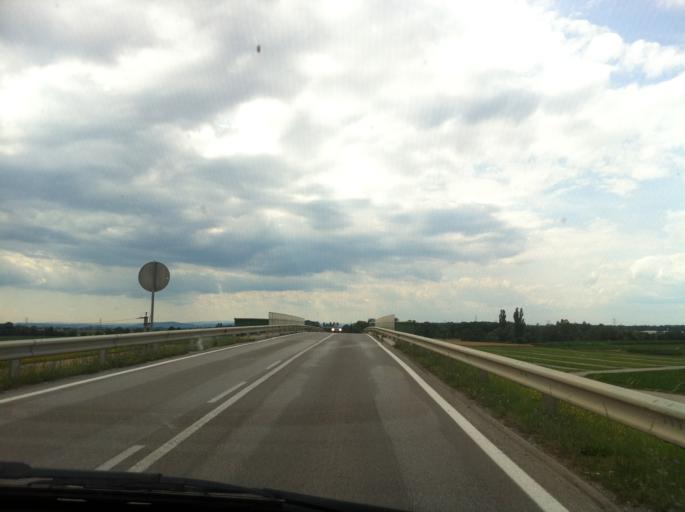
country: AT
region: Lower Austria
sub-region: Politischer Bezirk Tulln
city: Tulln
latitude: 48.3156
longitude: 16.0379
